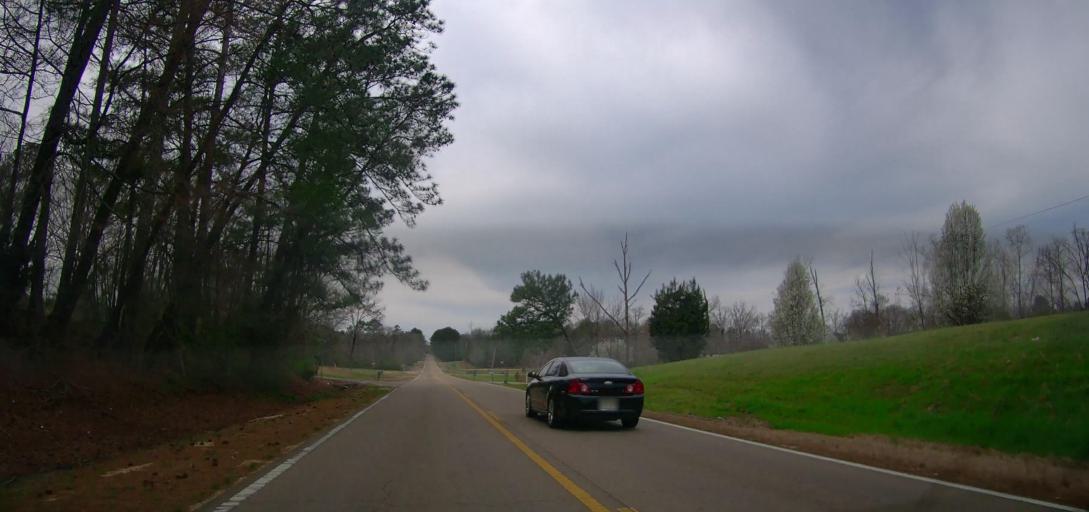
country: US
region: Mississippi
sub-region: Itawamba County
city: Mantachie
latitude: 34.2644
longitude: -88.5427
